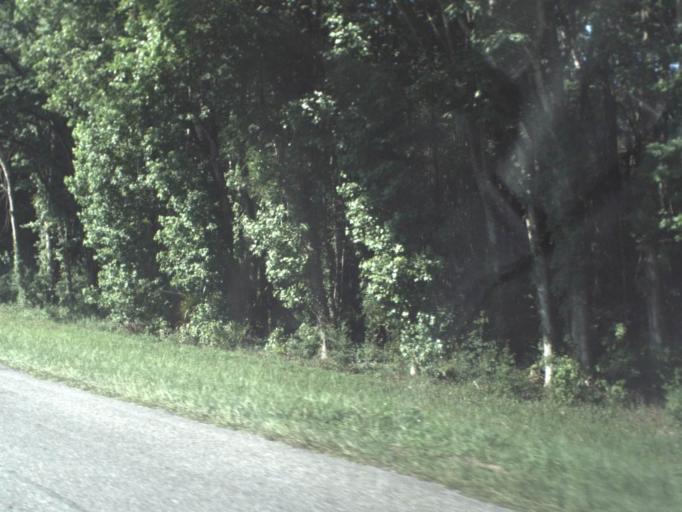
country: US
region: Florida
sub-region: Saint Johns County
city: Fruit Cove
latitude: 30.0249
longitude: -81.4854
